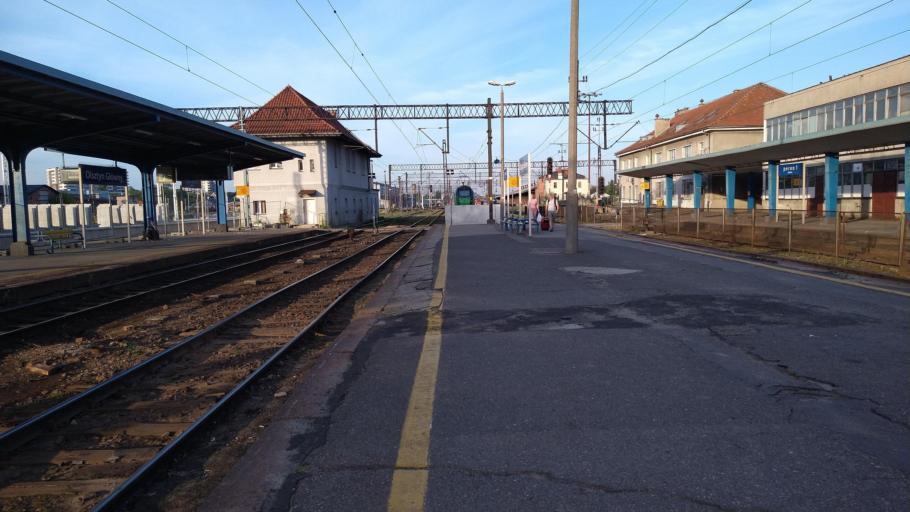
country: PL
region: Warmian-Masurian Voivodeship
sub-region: Powiat olsztynski
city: Olsztyn
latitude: 53.7859
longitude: 20.4984
